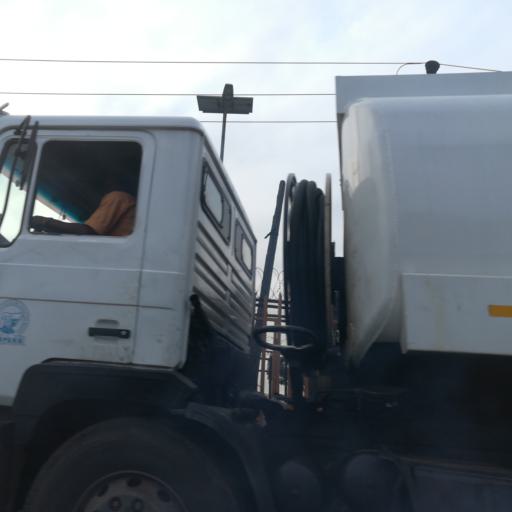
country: NG
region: Rivers
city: Port Harcourt
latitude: 4.8468
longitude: 7.0458
